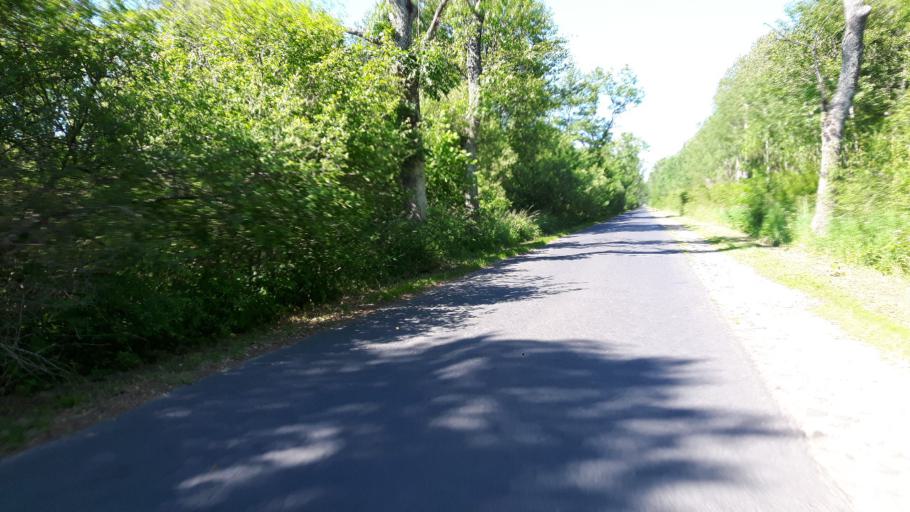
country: PL
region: Pomeranian Voivodeship
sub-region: Powiat slupski
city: Glowczyce
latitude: 54.6540
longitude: 17.4205
